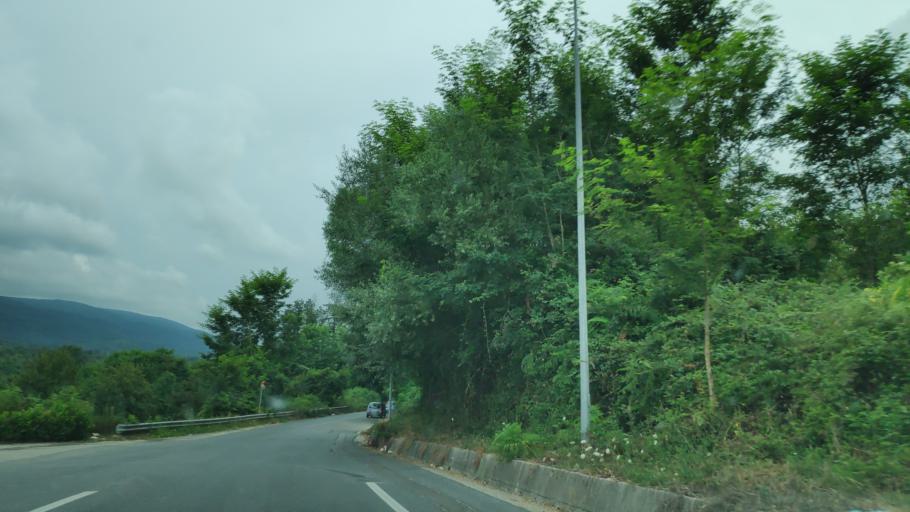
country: IT
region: Calabria
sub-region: Provincia di Vibo-Valentia
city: Brognaturo
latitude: 38.5891
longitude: 16.3365
